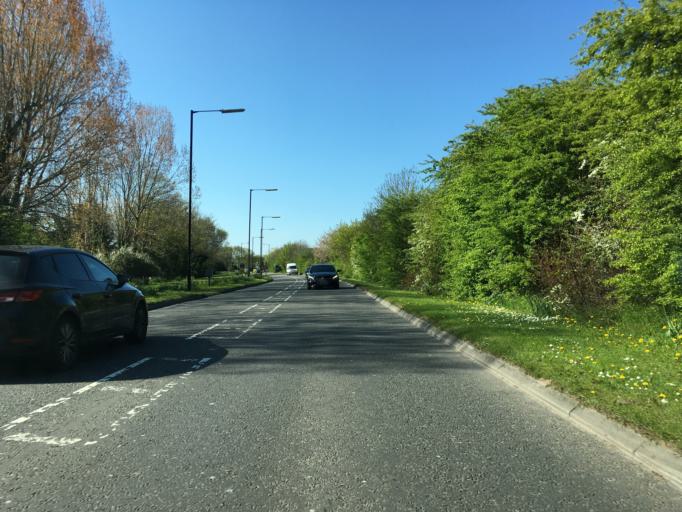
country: GB
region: England
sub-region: North Somerset
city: Portishead
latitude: 51.4793
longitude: -2.7571
